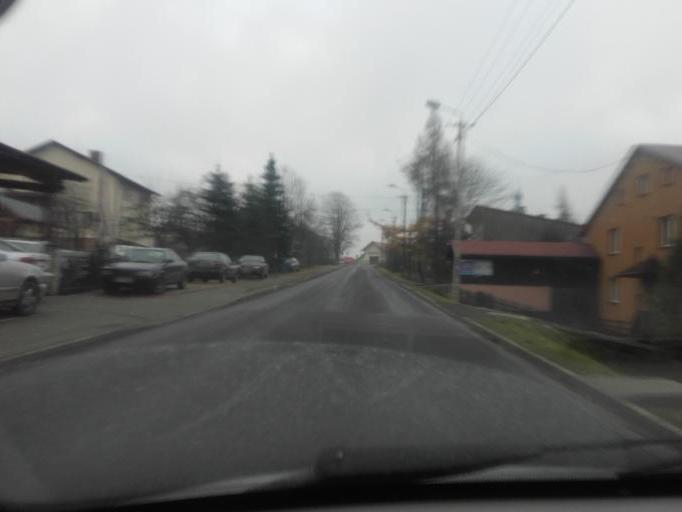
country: PL
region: Silesian Voivodeship
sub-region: Powiat cieszynski
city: Istebna
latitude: 49.5598
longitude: 18.9168
